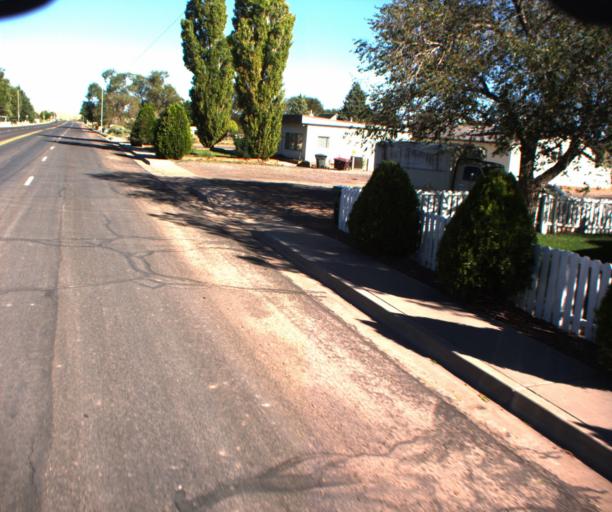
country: US
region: Arizona
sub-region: Navajo County
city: Joseph City
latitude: 34.9559
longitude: -110.3310
